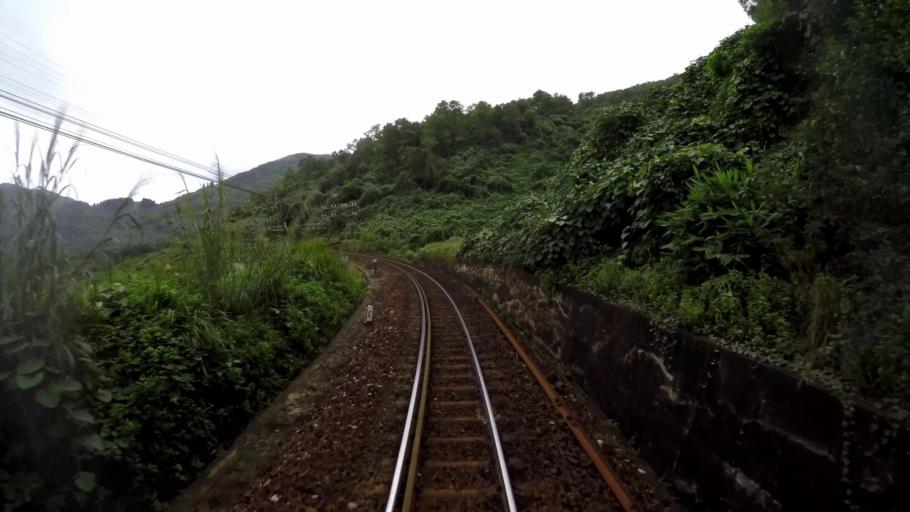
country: VN
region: Da Nang
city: Lien Chieu
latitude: 16.2119
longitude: 108.1363
